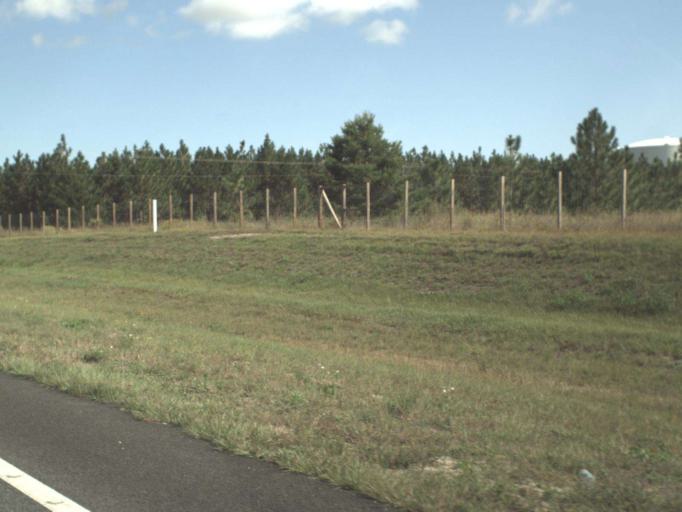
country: US
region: Florida
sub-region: Walton County
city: Freeport
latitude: 30.5731
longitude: -86.1079
